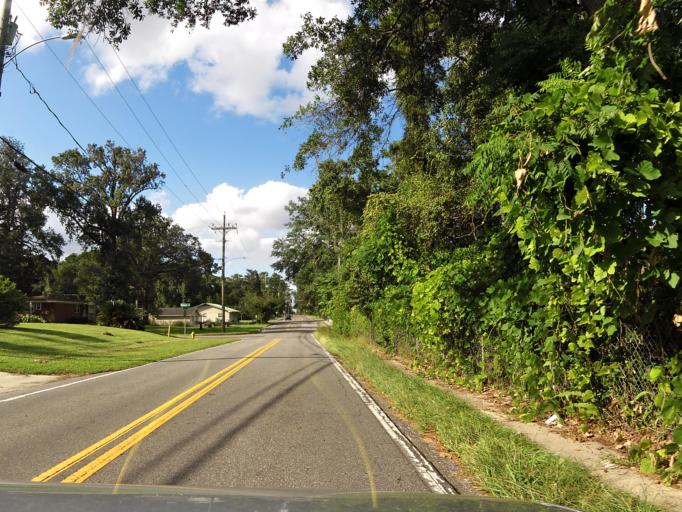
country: US
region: Florida
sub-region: Duval County
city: Jacksonville
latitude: 30.2905
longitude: -81.7388
